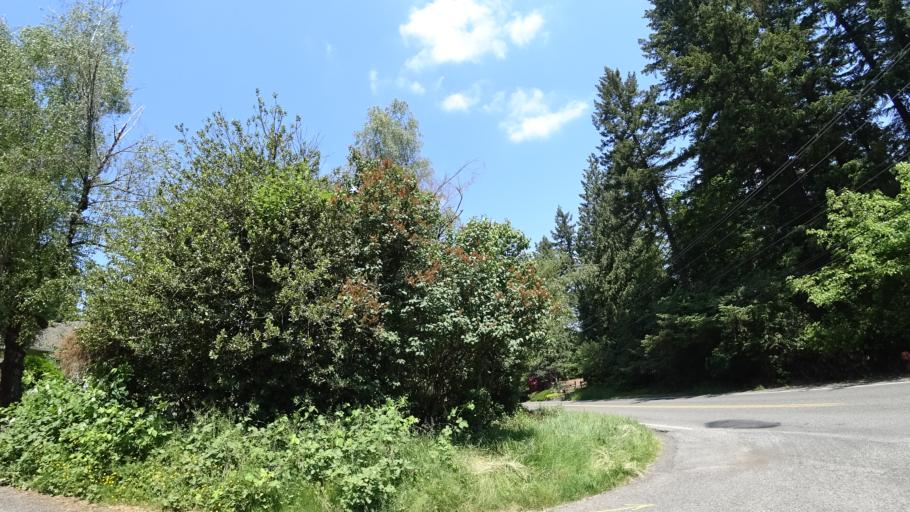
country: US
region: Oregon
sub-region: Washington County
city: Metzger
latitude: 45.4426
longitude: -122.7130
